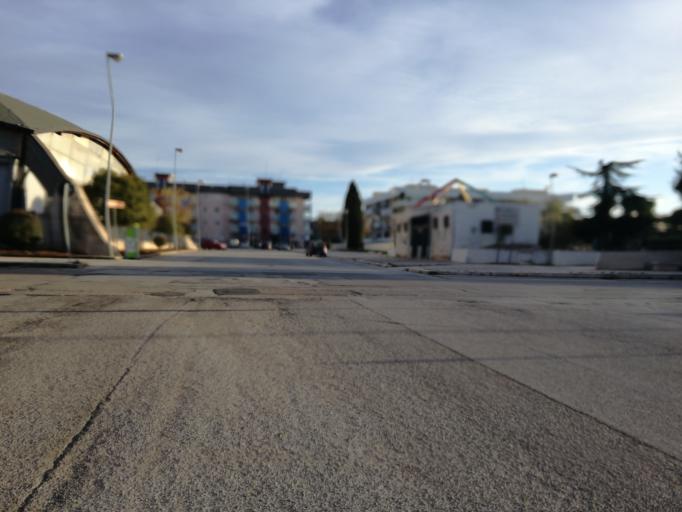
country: IT
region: Apulia
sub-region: Provincia di Bari
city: Valenzano
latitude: 41.0467
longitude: 16.8880
